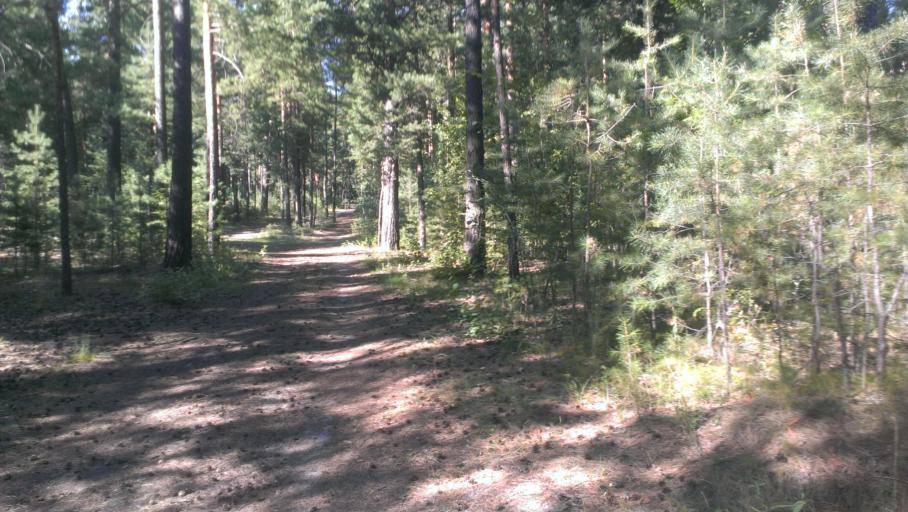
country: RU
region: Altai Krai
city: Novosilikatnyy
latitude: 53.3154
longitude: 83.6850
